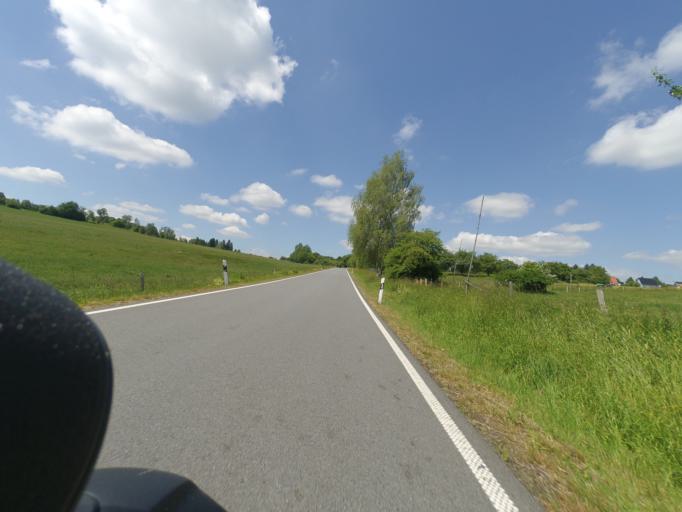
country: DE
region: Saxony
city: Hohnstein
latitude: 50.9781
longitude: 14.1312
